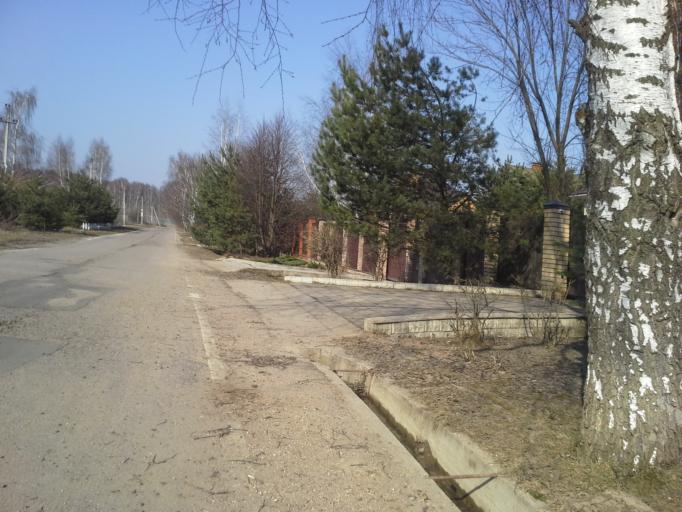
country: RU
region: Moscow
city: Tolstopal'tsevo
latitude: 55.6245
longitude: 37.2215
